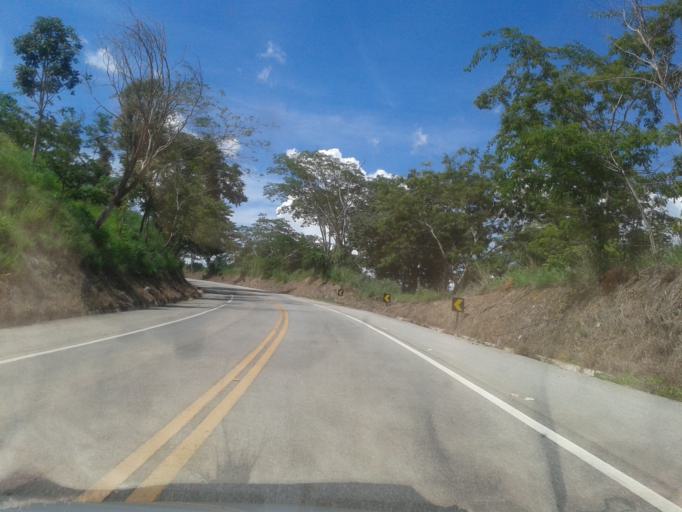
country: BR
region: Goias
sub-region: Goias
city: Goias
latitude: -15.7850
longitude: -50.1313
